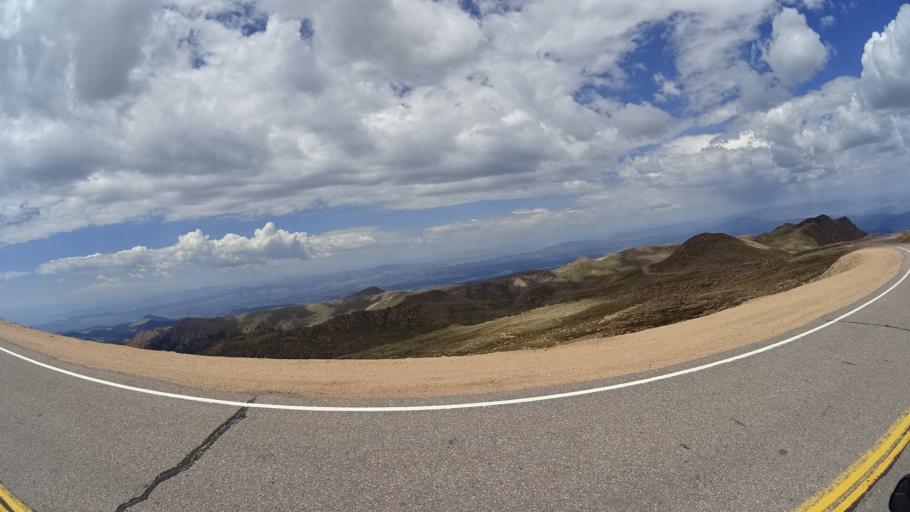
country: US
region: Colorado
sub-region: El Paso County
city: Cascade-Chipita Park
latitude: 38.8425
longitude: -105.0495
